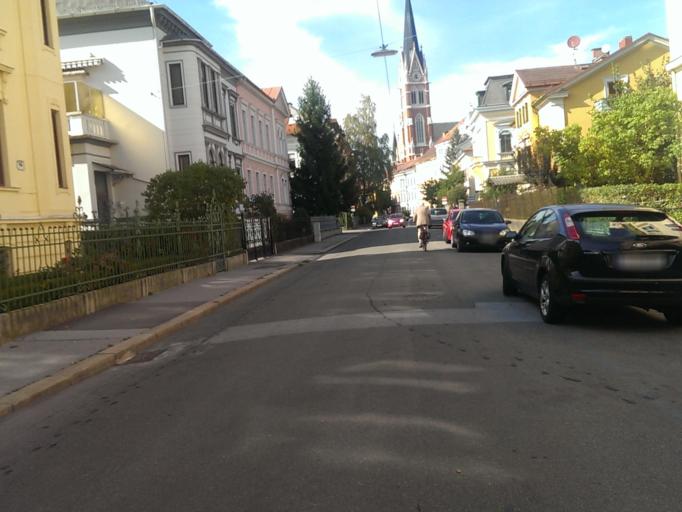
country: AT
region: Styria
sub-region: Graz Stadt
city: Graz
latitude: 47.0670
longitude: 15.4574
